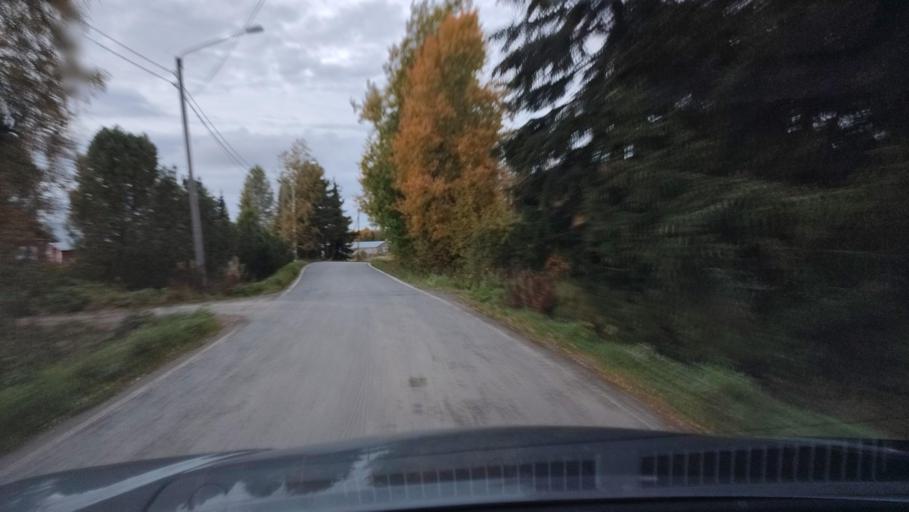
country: FI
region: Ostrobothnia
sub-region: Sydosterbotten
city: Kristinestad
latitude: 62.2669
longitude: 21.5092
